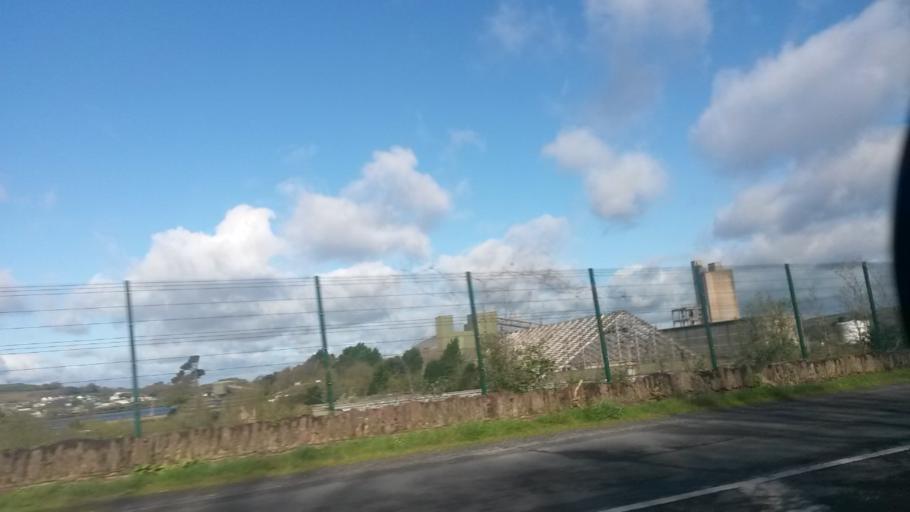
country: IE
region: Munster
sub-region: County Cork
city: Passage West
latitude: 51.8752
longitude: -8.3241
